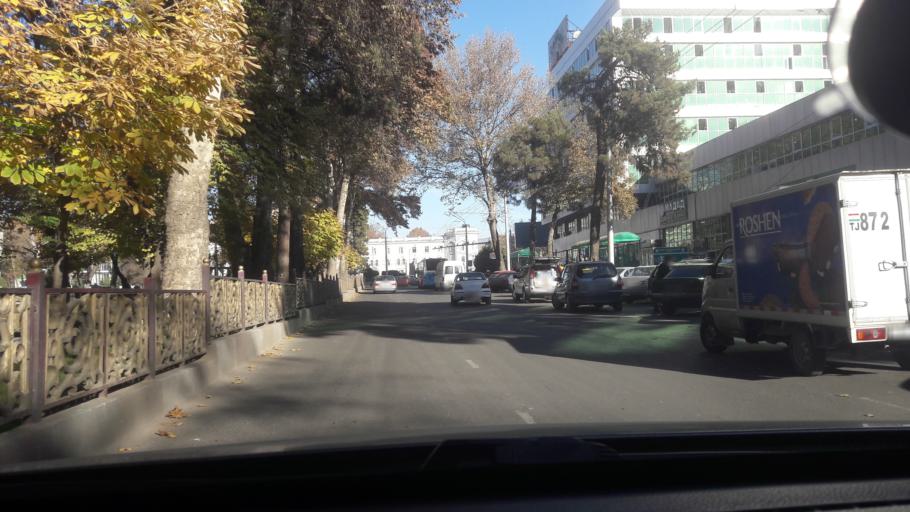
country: TJ
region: Dushanbe
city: Dushanbe
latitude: 38.5610
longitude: 68.7995
